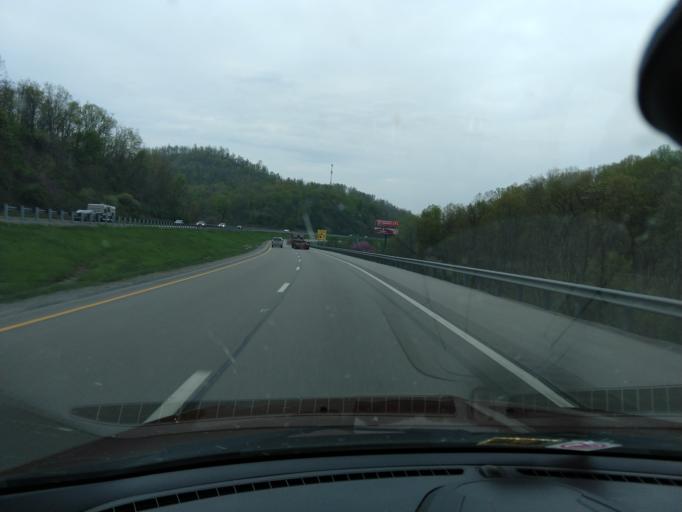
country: US
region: West Virginia
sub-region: Harrison County
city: Stonewood
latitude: 39.1453
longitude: -80.3632
